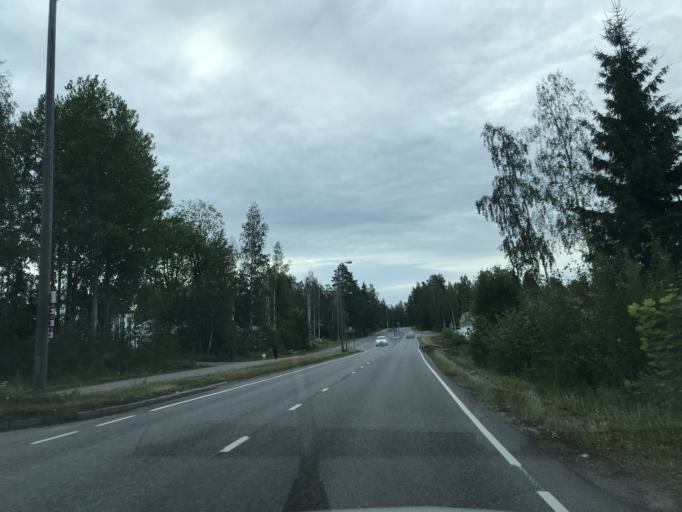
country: FI
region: Uusimaa
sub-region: Helsinki
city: Nurmijaervi
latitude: 60.3836
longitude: 24.6878
